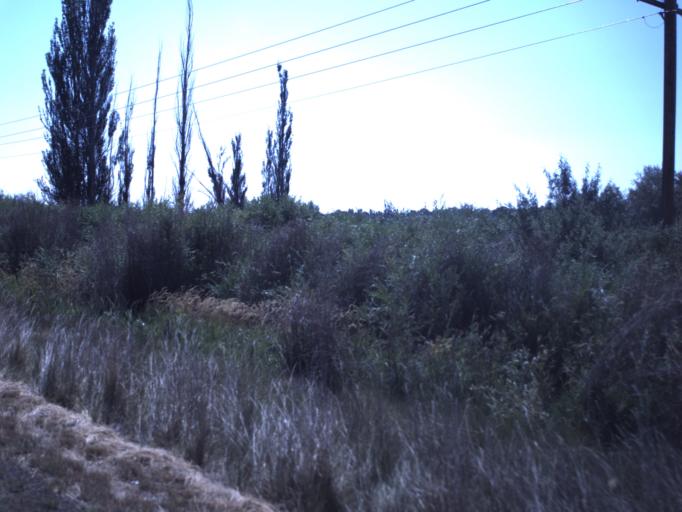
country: US
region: Utah
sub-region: Duchesne County
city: Roosevelt
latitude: 40.2580
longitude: -110.1696
